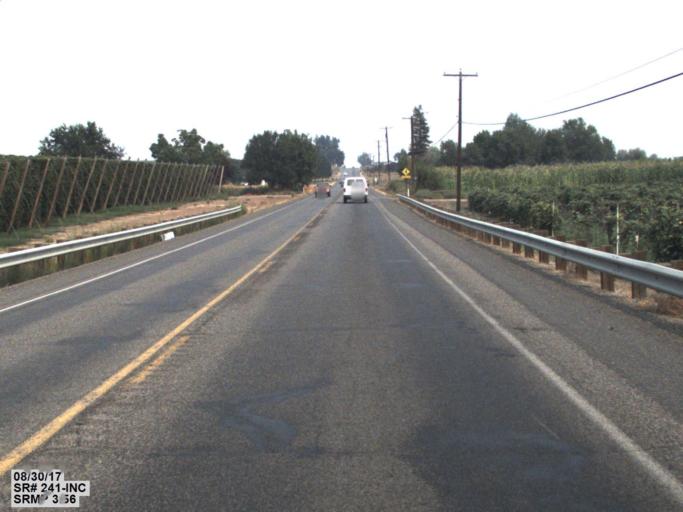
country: US
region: Washington
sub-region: Yakima County
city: Mabton
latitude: 46.2631
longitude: -119.9994
